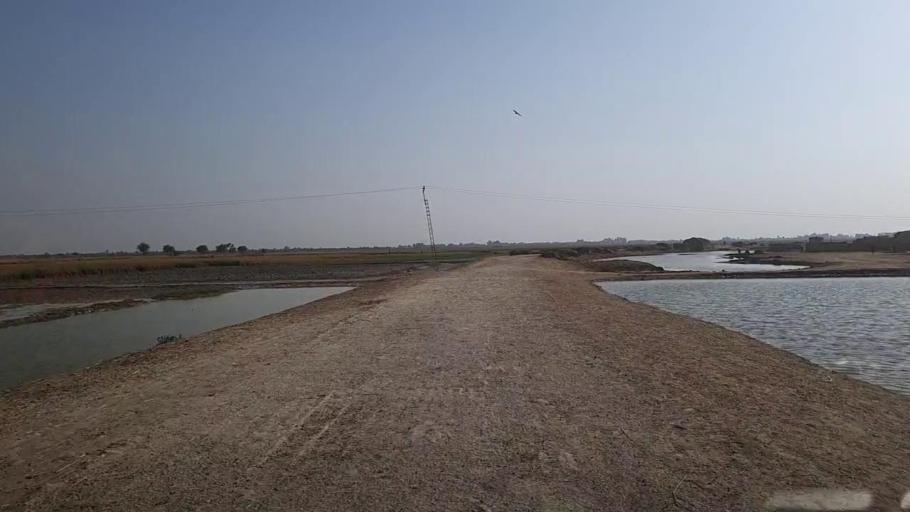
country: PK
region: Sindh
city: Kandhkot
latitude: 28.3703
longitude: 69.3330
